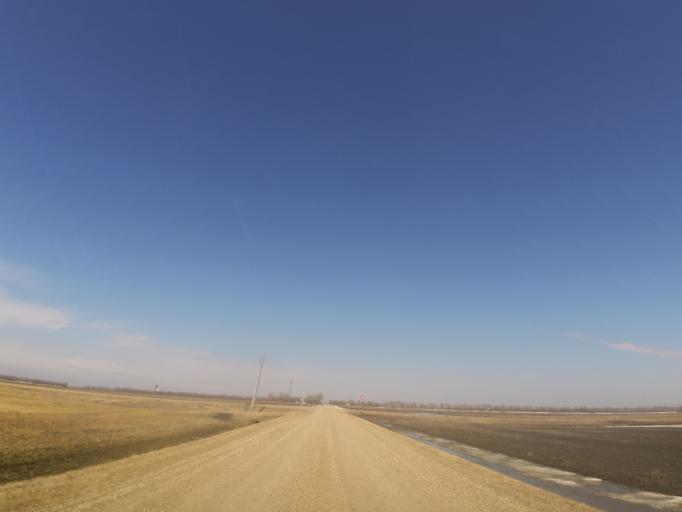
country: US
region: North Dakota
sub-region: Walsh County
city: Grafton
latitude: 48.4256
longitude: -97.2122
